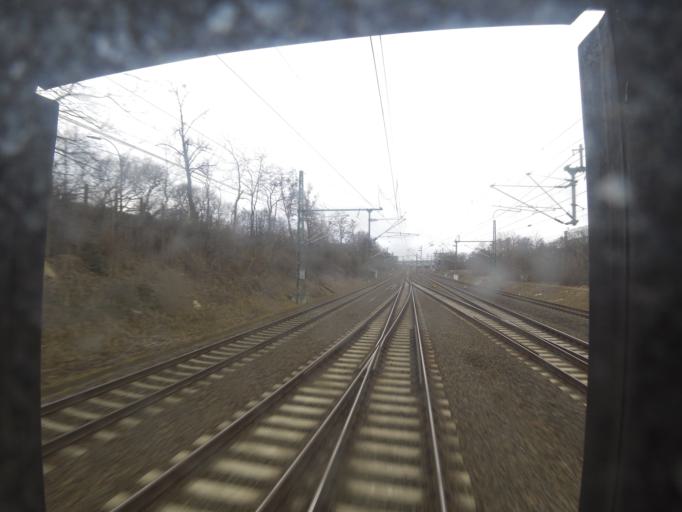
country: DE
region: Berlin
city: Berlin Schoeneberg
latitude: 52.4839
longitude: 13.3706
